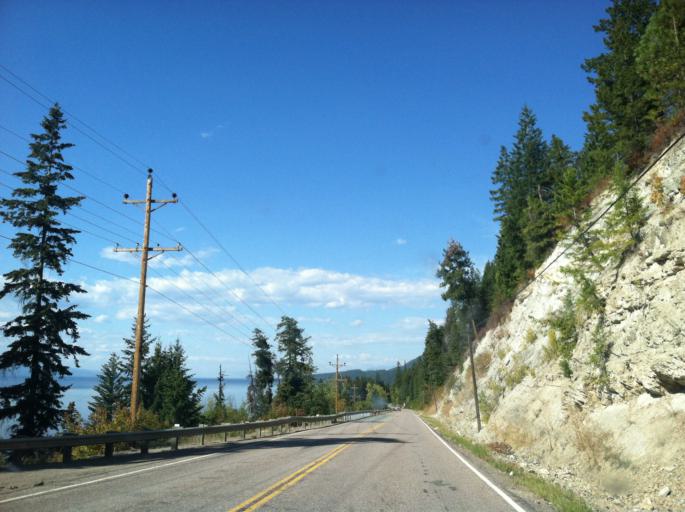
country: US
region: Montana
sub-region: Lake County
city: Polson
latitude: 47.7258
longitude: -114.0385
